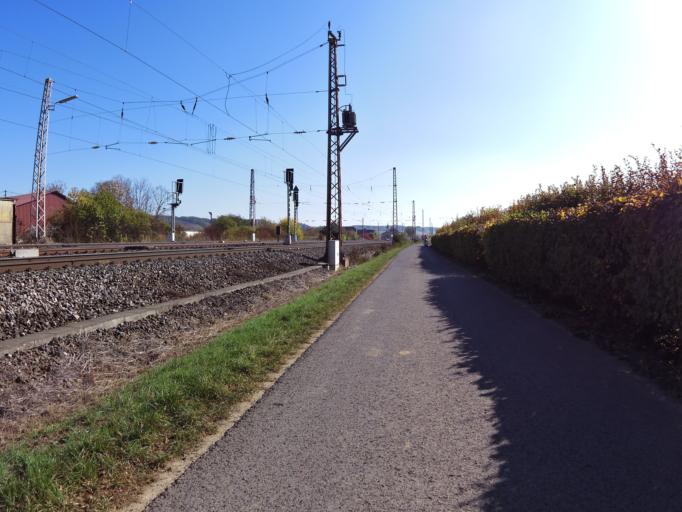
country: DE
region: Bavaria
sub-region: Regierungsbezirk Unterfranken
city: Winterhausen
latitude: 49.7125
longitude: 10.0063
